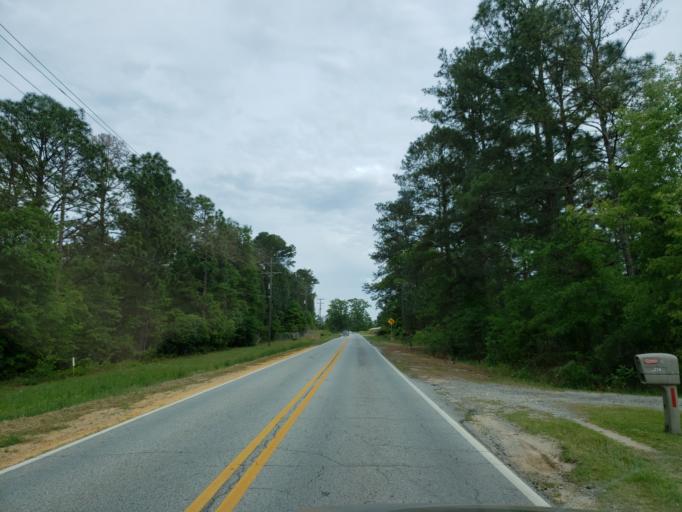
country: US
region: Georgia
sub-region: Bibb County
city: West Point
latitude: 32.7491
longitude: -83.7399
